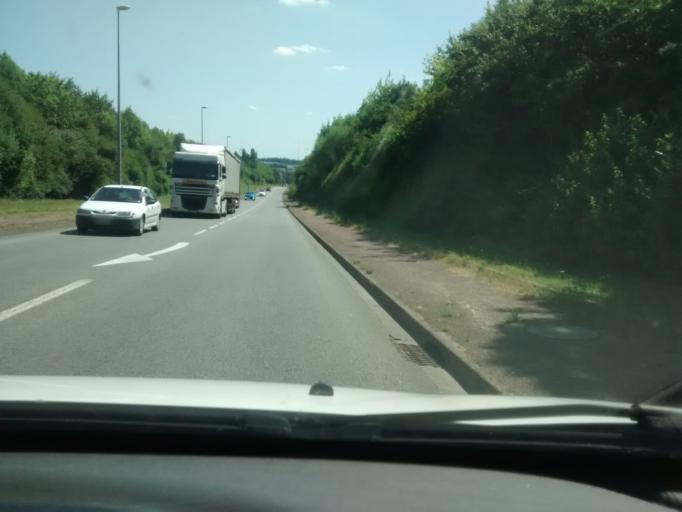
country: FR
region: Brittany
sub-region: Departement d'Ille-et-Vilaine
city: Cesson-Sevigne
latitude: 48.1215
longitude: -1.6208
